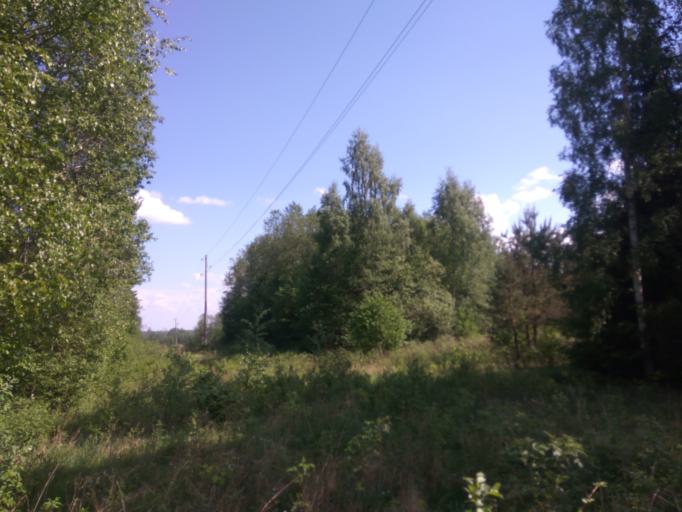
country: LV
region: Kuldigas Rajons
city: Kuldiga
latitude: 57.1749
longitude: 22.0180
